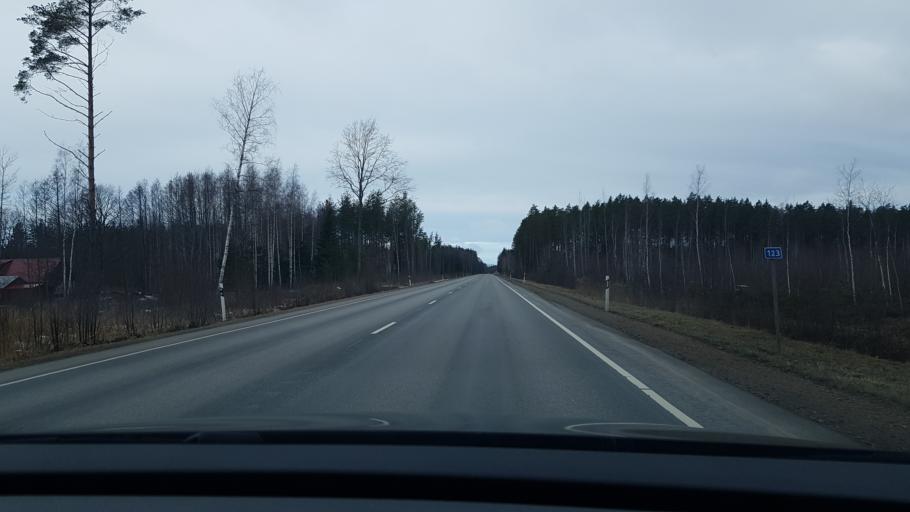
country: EE
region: Paernumaa
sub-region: Paikuse vald
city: Paikuse
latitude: 58.2801
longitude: 24.6164
